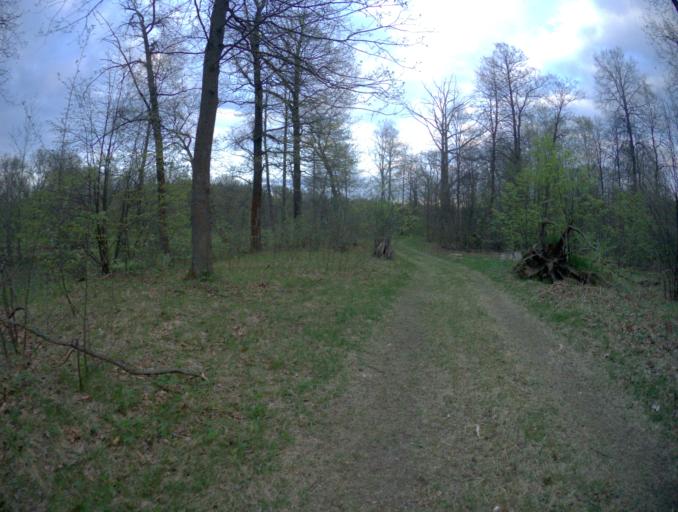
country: RU
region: Vladimir
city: Raduzhnyy
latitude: 56.0445
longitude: 40.3782
